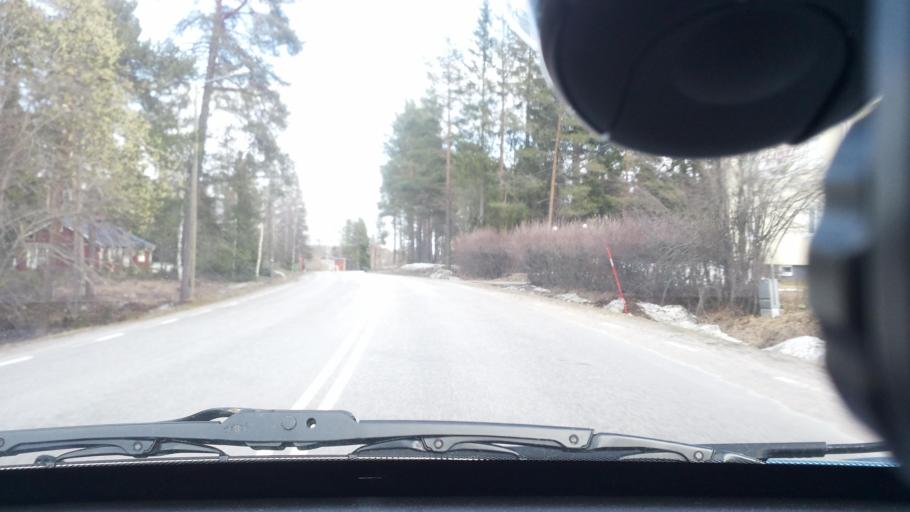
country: SE
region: Norrbotten
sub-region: Lulea Kommun
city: Gammelstad
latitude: 65.5873
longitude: 22.0186
